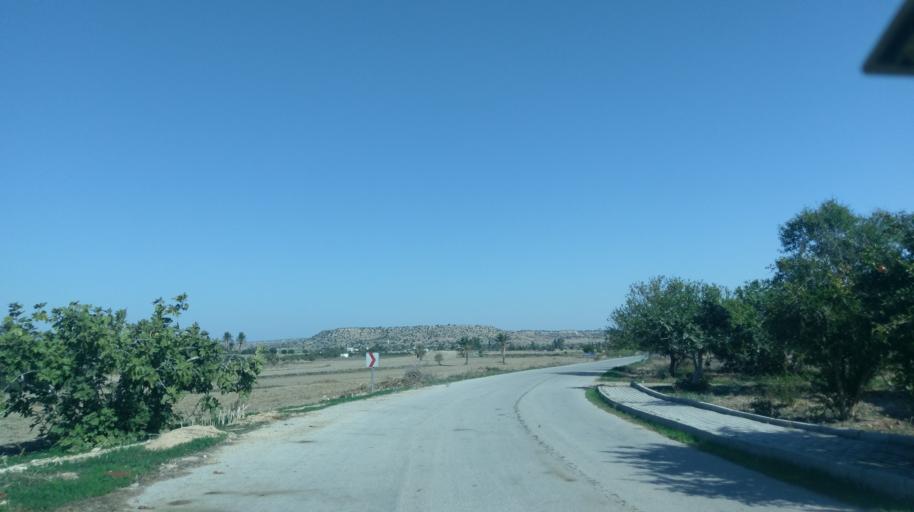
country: CY
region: Ammochostos
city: Leonarisso
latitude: 35.3902
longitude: 34.0157
